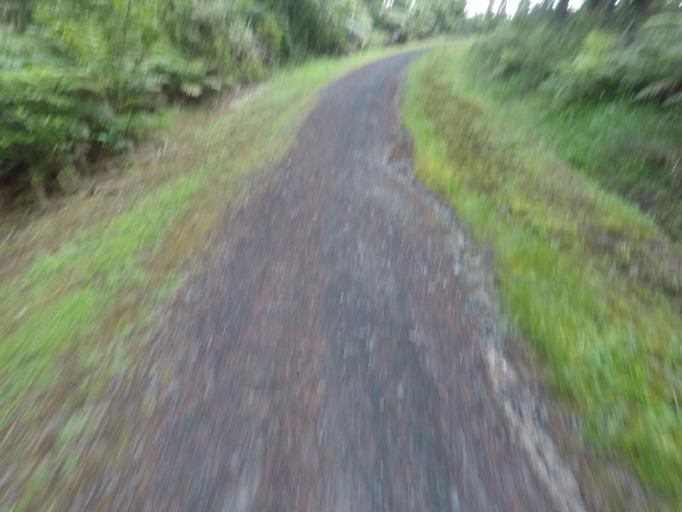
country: NZ
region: Auckland
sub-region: Auckland
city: Parakai
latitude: -36.7085
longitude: 174.5789
